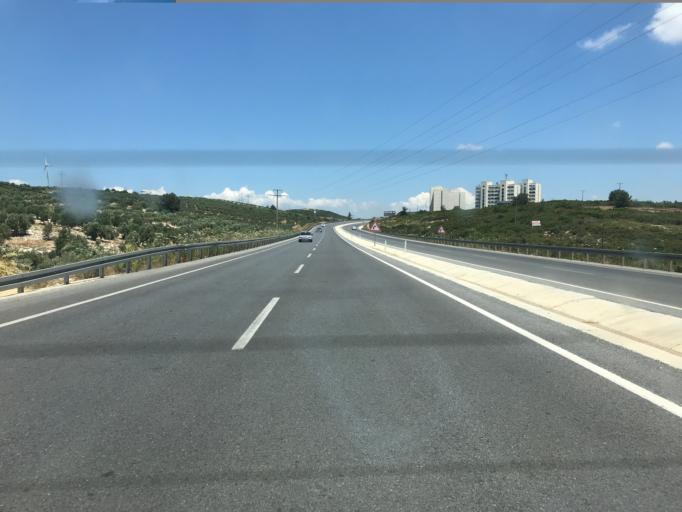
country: TR
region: Aydin
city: Akkoy
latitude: 37.4714
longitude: 27.3393
